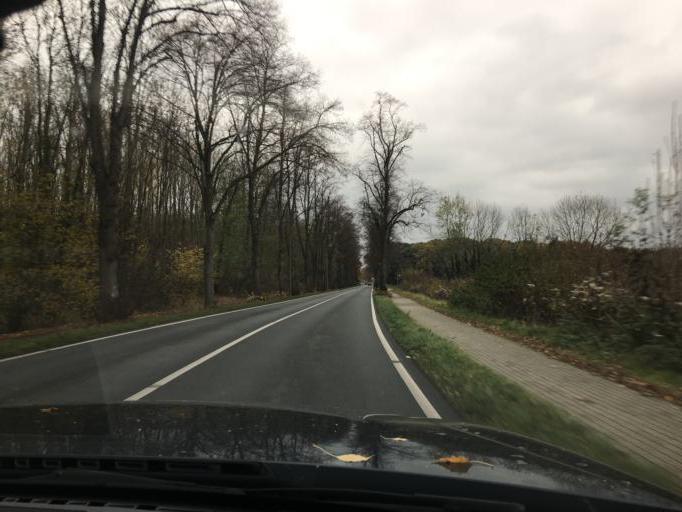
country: DE
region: North Rhine-Westphalia
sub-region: Regierungsbezirk Munster
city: Muenster
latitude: 51.9900
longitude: 7.6816
